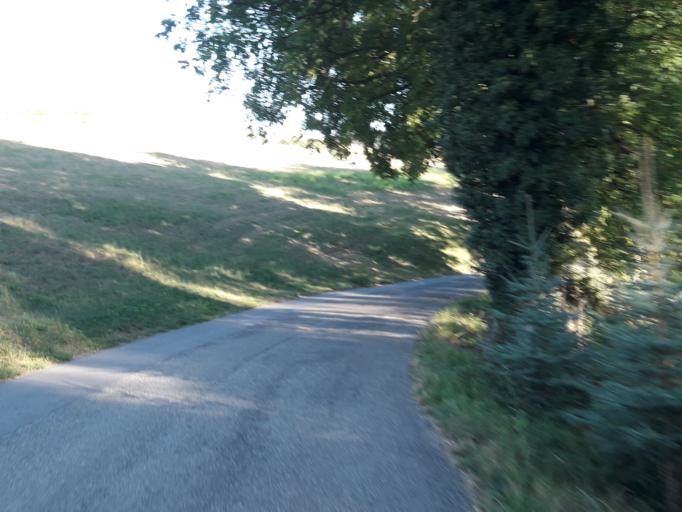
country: CH
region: Aargau
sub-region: Bezirk Baden
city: Unterehrendingen
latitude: 47.5613
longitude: 8.3600
